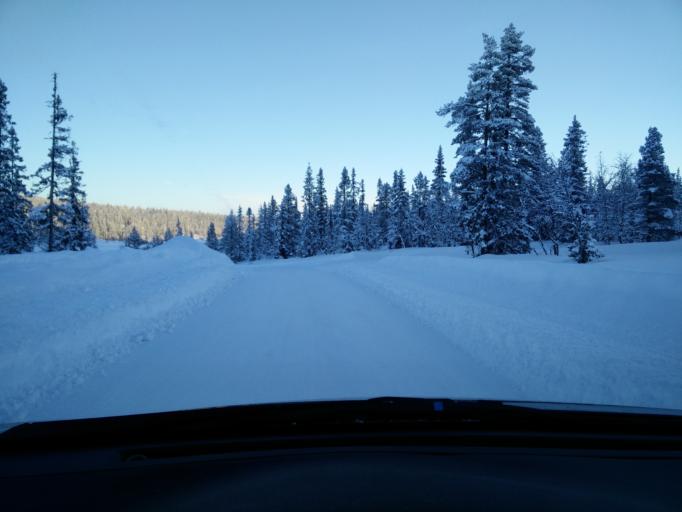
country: SE
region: Jaemtland
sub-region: Bergs Kommun
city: Hoverberg
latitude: 62.4995
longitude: 14.1105
